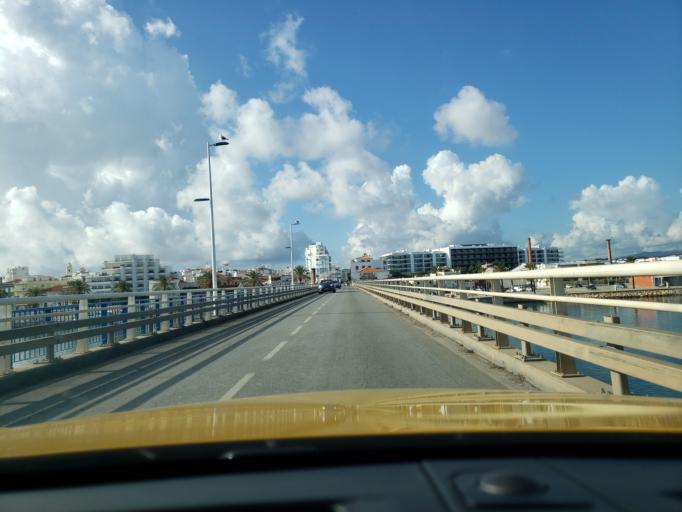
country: PT
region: Faro
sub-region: Portimao
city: Portimao
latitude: 37.1392
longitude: -8.5302
